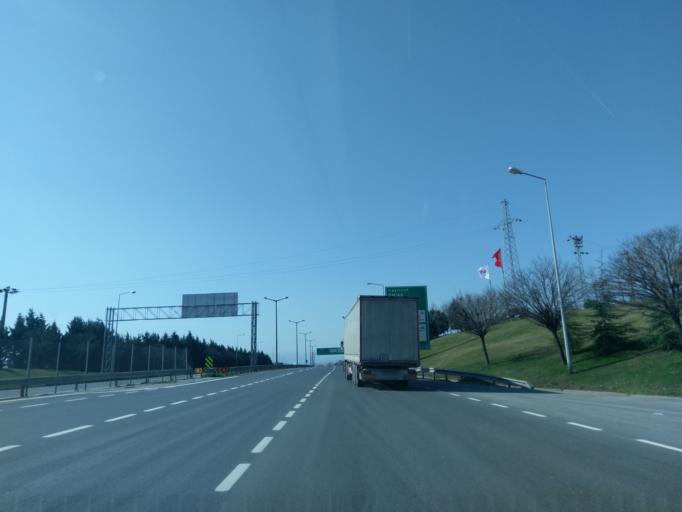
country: TR
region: Kocaeli
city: Balcik
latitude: 40.8670
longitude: 29.3889
